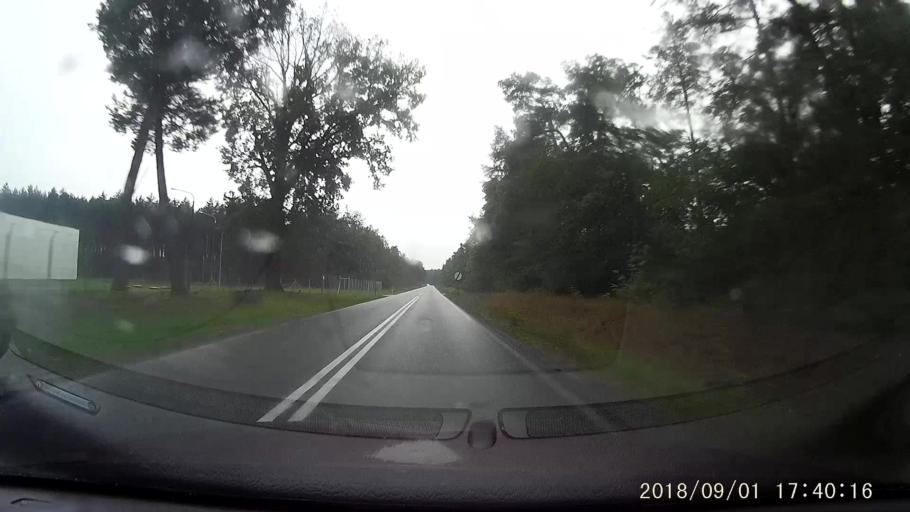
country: PL
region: Lubusz
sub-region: Powiat zaganski
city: Zagan
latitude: 51.5816
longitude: 15.2752
